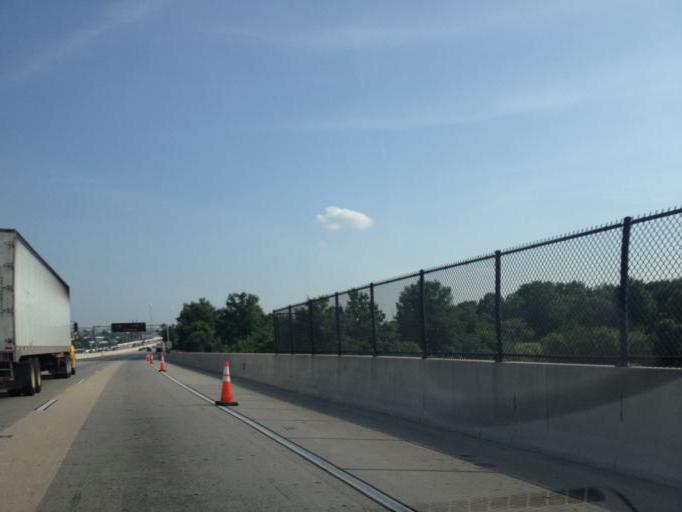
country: US
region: Maryland
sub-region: Baltimore County
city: Rosedale
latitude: 39.3056
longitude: -76.5310
